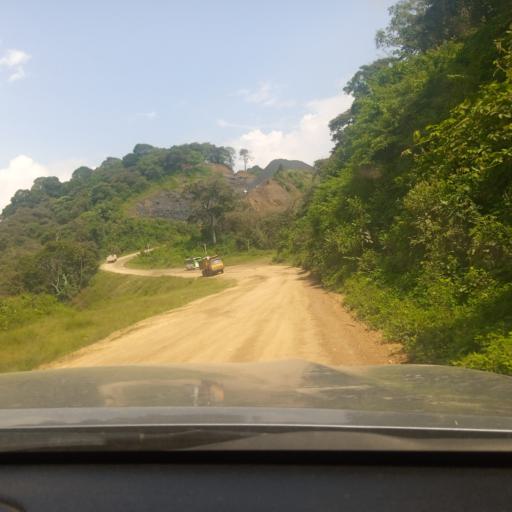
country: ET
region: Southern Nations, Nationalities, and People's Region
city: Tippi
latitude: 7.0698
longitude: 35.4380
